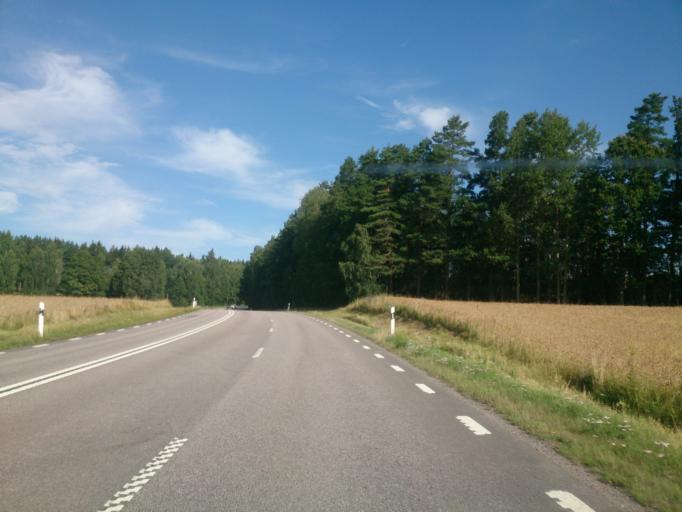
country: SE
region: OEstergoetland
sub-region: Atvidabergs Kommun
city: Atvidaberg
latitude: 58.2600
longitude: 15.9273
